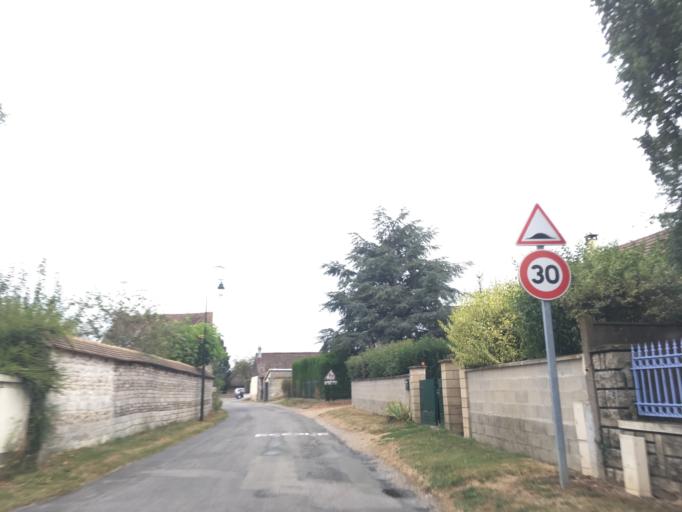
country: FR
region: Ile-de-France
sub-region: Departement des Yvelines
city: Limetz-Villez
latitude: 49.1034
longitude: 1.5353
